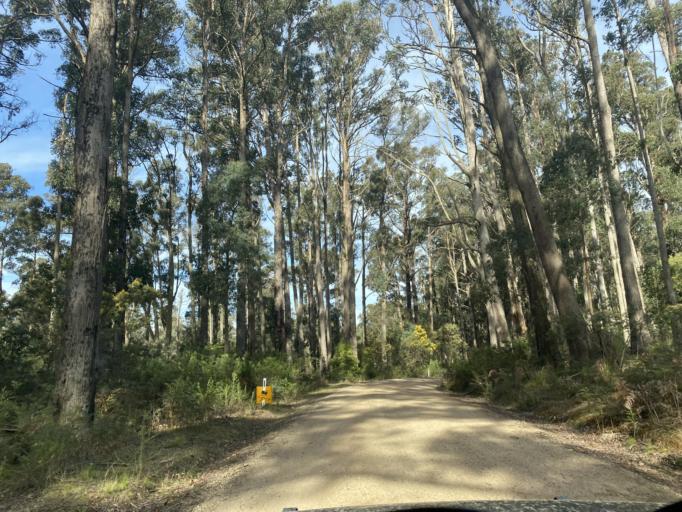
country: AU
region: Victoria
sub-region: Mansfield
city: Mansfield
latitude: -36.8488
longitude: 146.1818
